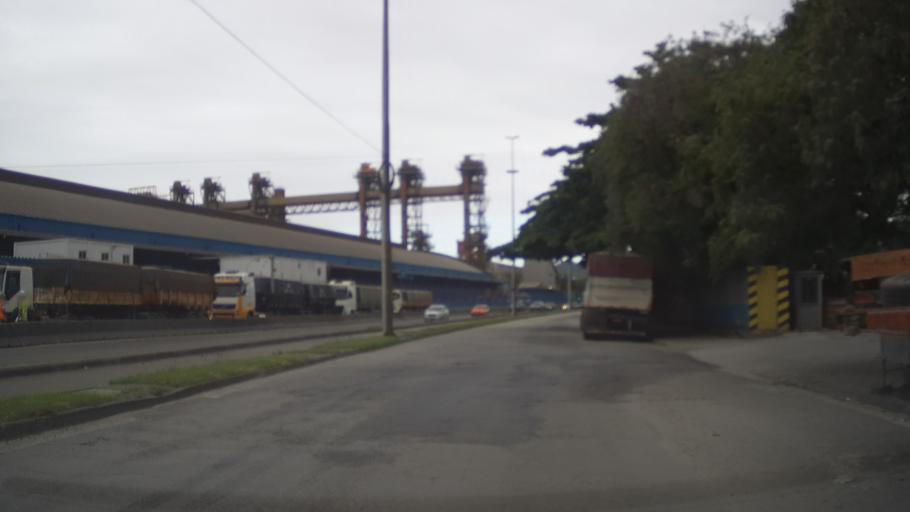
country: BR
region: Sao Paulo
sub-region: Guaruja
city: Guaruja
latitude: -23.9797
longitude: -46.2940
